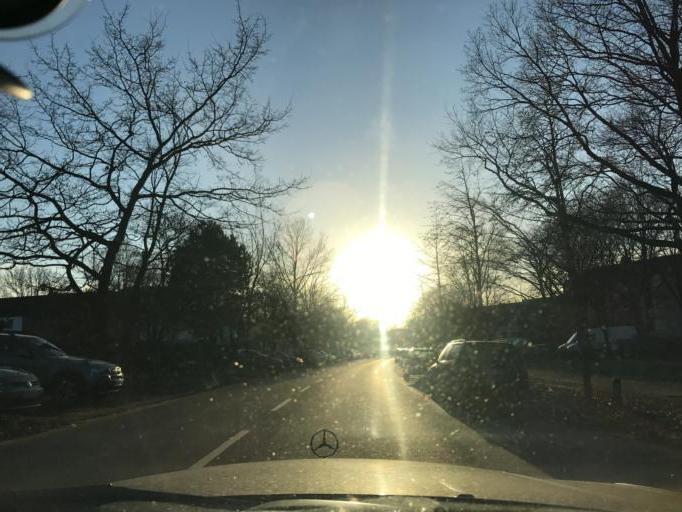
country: DE
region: Hamburg
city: Steilshoop
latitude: 53.6048
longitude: 10.0870
